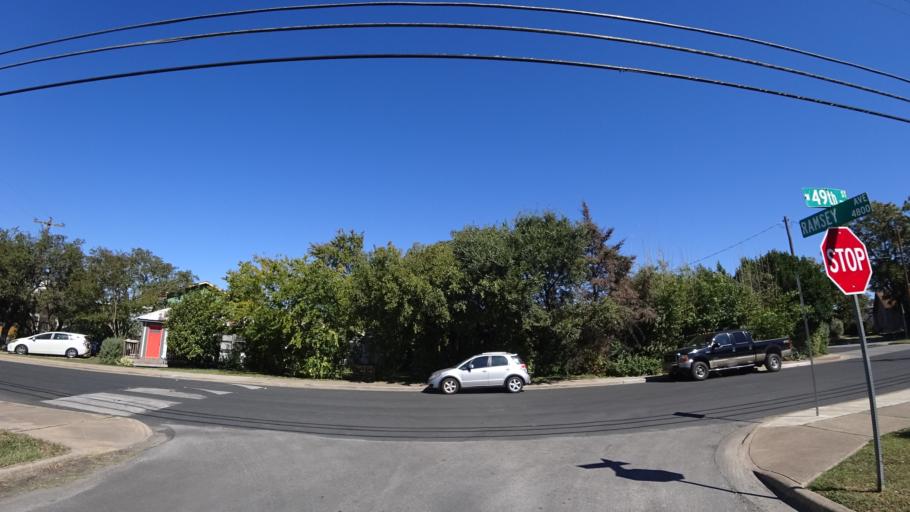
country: US
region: Texas
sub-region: Travis County
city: Austin
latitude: 30.3207
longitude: -97.7408
